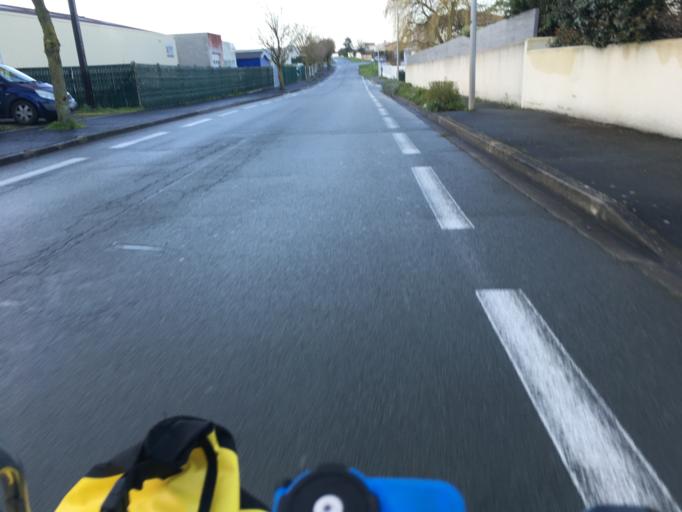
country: FR
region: Poitou-Charentes
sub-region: Departement de la Charente-Maritime
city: Nieul-sur-Mer
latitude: 46.2026
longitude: -1.1717
